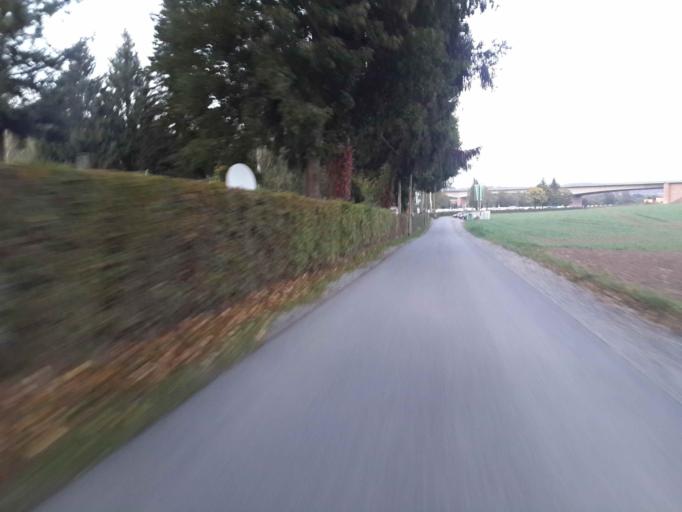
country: DE
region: Bavaria
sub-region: Regierungsbezirk Unterfranken
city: Kreuzwertheim
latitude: 49.7802
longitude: 9.5650
